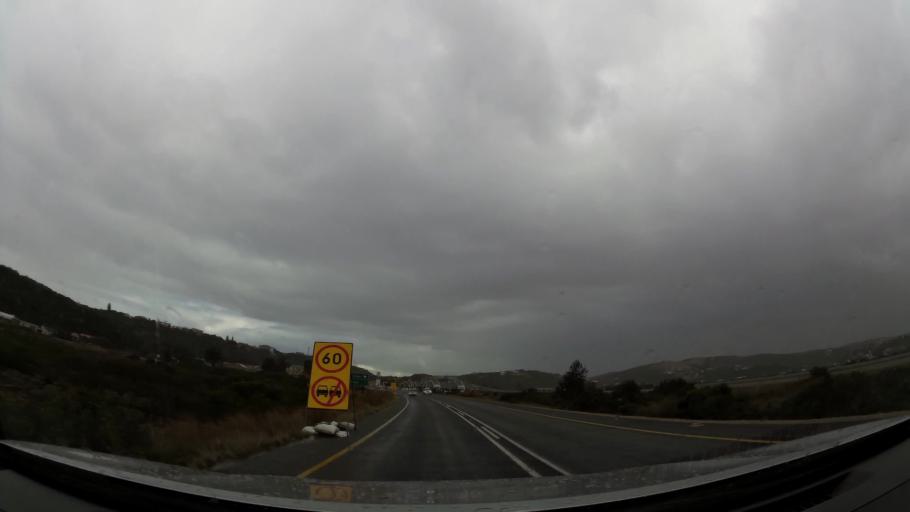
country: ZA
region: Western Cape
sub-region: Eden District Municipality
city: Mossel Bay
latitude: -34.0524
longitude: 22.2290
